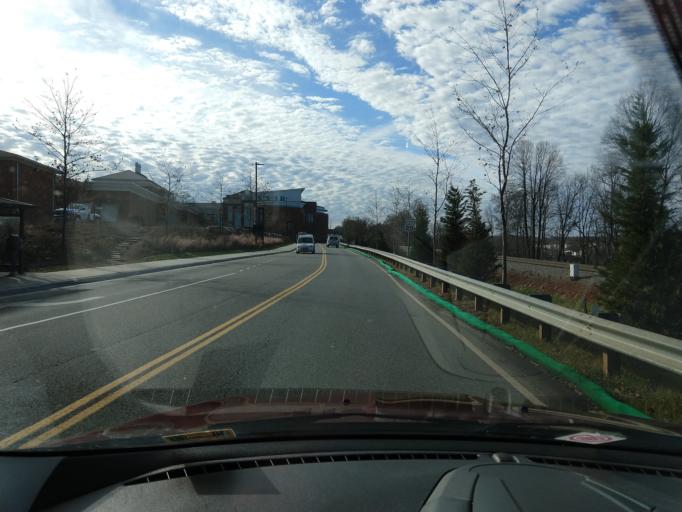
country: US
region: Virginia
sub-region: City of Lynchburg
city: West Lynchburg
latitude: 37.3533
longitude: -79.1819
